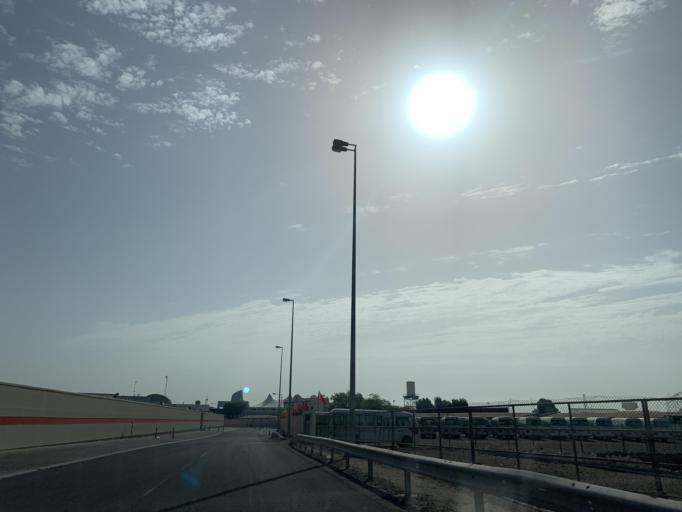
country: BH
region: Northern
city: Sitrah
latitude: 26.1679
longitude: 50.6003
